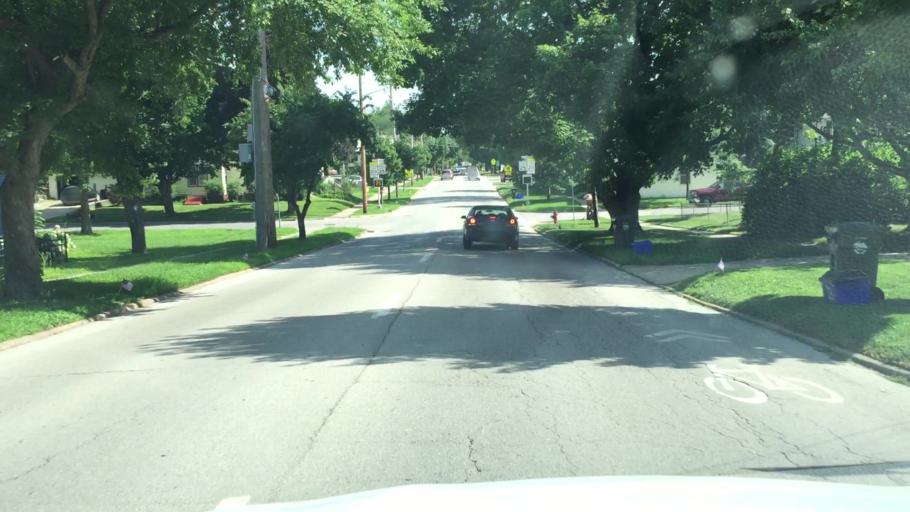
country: US
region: Iowa
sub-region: Johnson County
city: Iowa City
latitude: 41.6695
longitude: -91.5257
